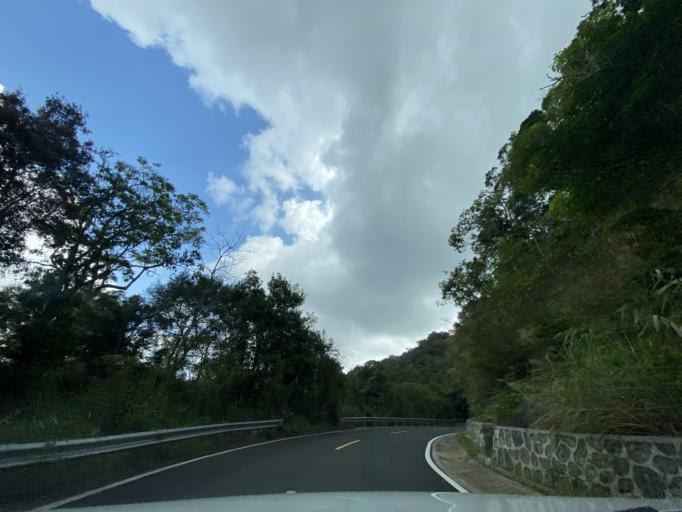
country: CN
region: Hainan
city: Diaoluoshan
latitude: 18.7114
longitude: 109.8818
